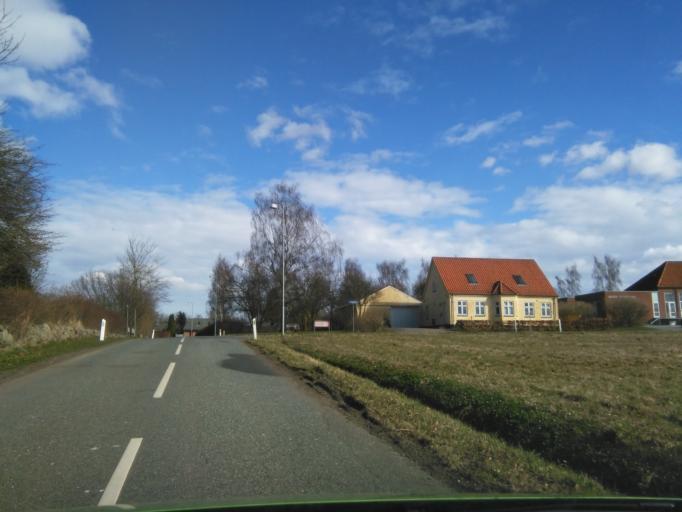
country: DK
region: Central Jutland
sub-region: Skanderborg Kommune
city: Skanderborg
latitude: 55.9205
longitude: 9.9958
